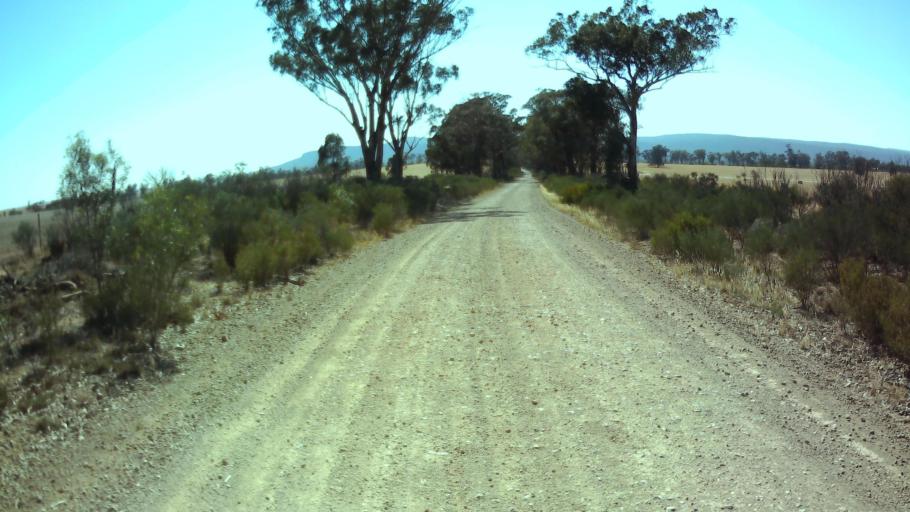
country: AU
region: New South Wales
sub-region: Weddin
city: Grenfell
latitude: -33.9016
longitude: 147.8674
